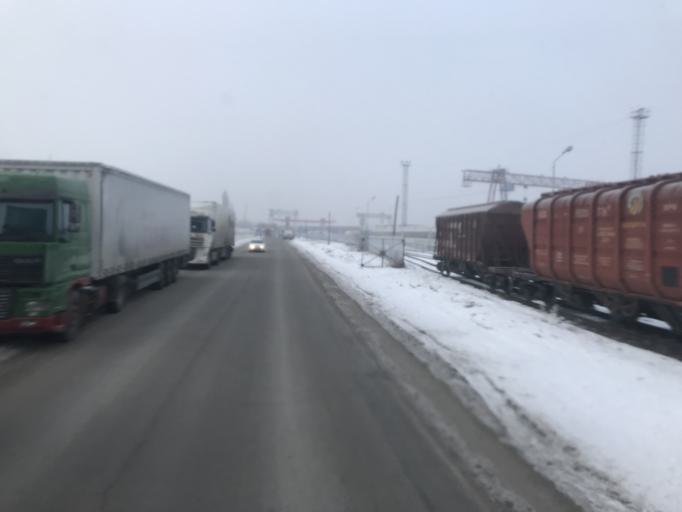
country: KZ
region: Almaty Oblysy
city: Pervomayskiy
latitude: 43.3600
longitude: 76.9760
